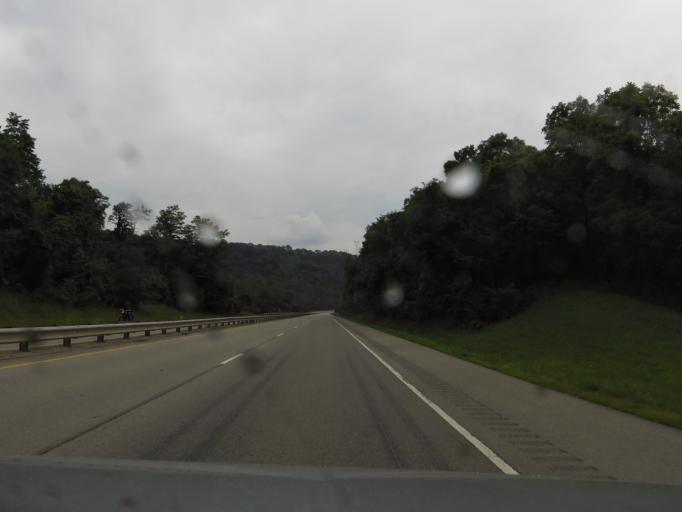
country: US
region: Ohio
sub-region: Brown County
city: Ripley
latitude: 38.7696
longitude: -83.8137
